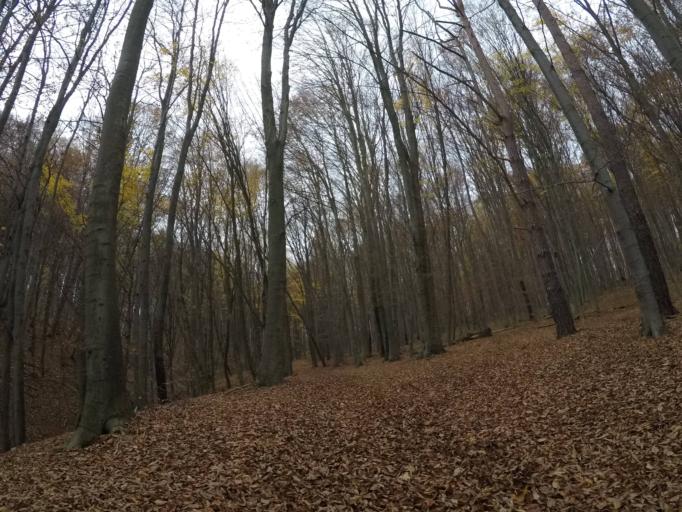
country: SK
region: Presovsky
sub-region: Okres Presov
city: Presov
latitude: 48.9671
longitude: 21.1887
